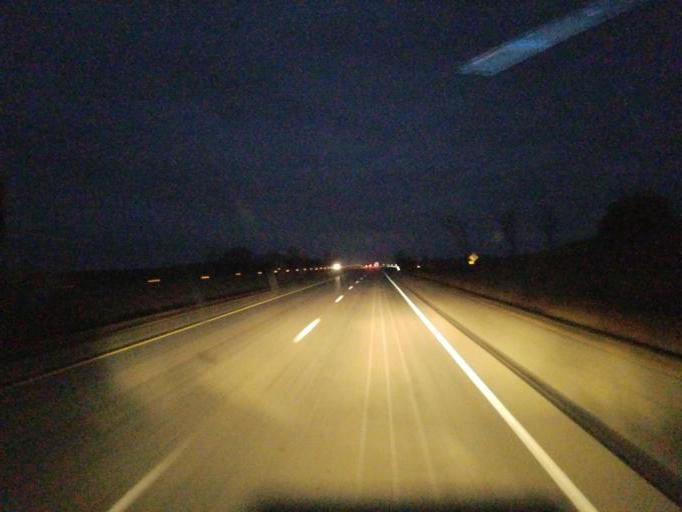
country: US
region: Iowa
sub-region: Guthrie County
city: Guthrie Center
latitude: 41.4960
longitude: -94.5030
